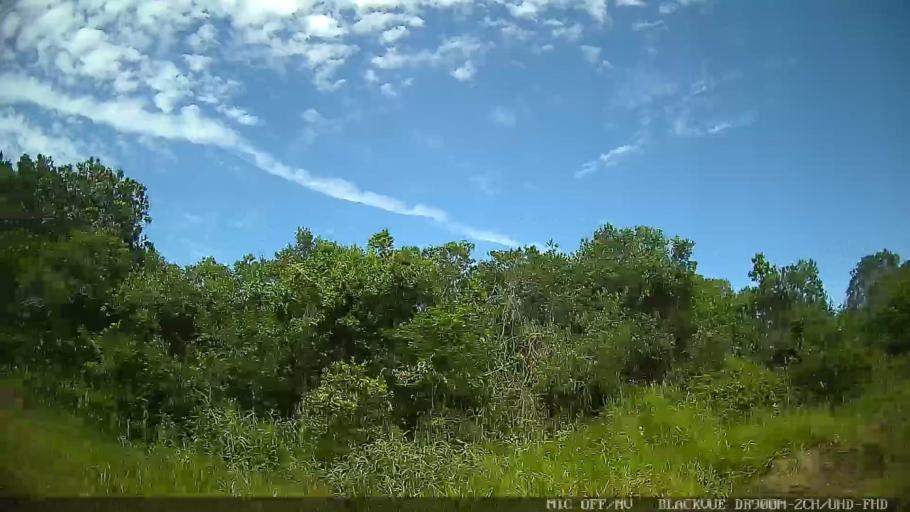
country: BR
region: Sao Paulo
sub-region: Iguape
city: Iguape
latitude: -24.7152
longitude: -47.5139
